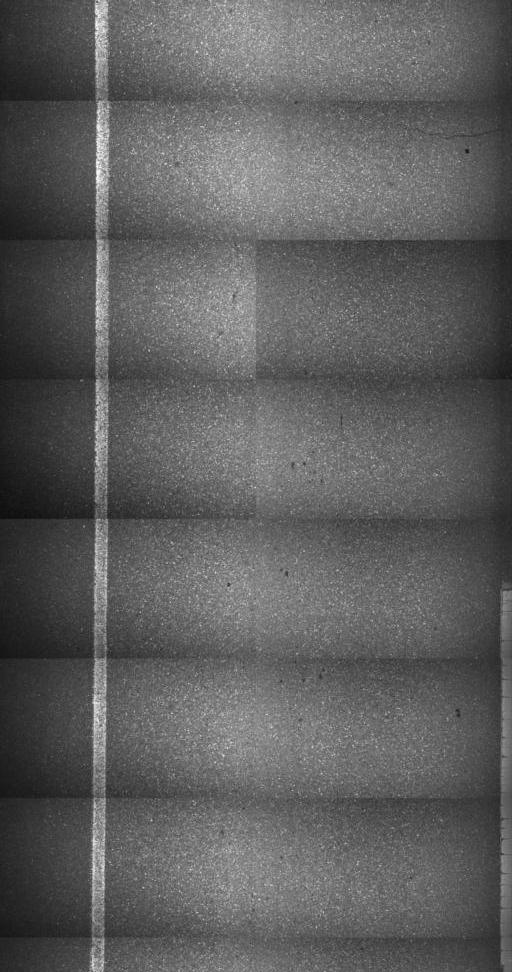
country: US
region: Vermont
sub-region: Orleans County
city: Newport
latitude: 44.6934
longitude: -72.1918
